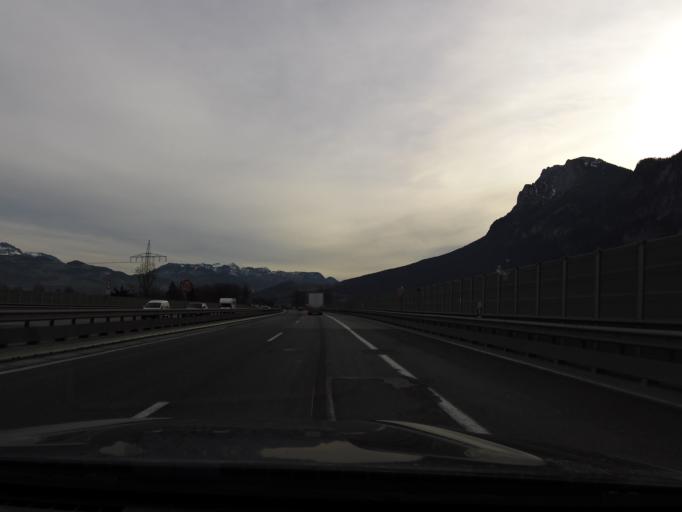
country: DE
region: Bavaria
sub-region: Upper Bavaria
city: Kiefersfelden
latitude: 47.6046
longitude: 12.1931
